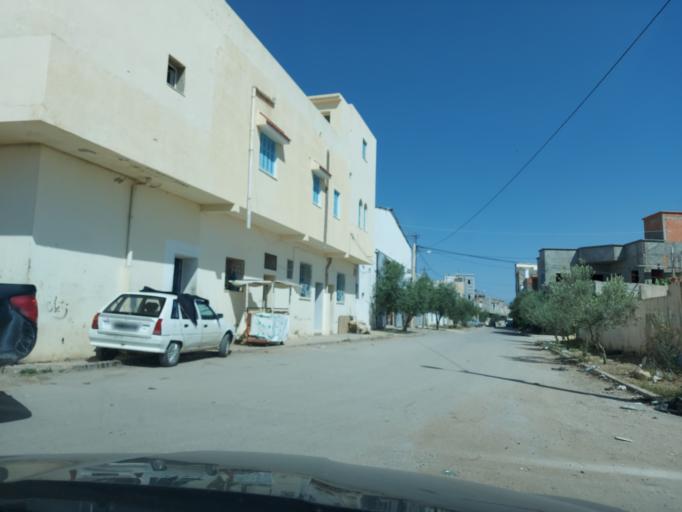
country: TN
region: Silyanah
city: Siliana
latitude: 36.0912
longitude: 9.3777
